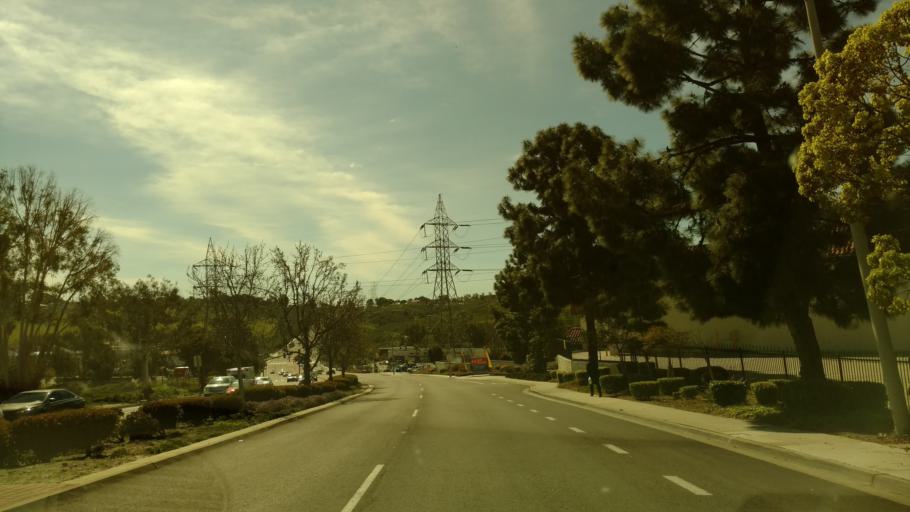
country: US
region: California
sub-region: San Diego County
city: Oceanside
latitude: 33.2035
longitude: -117.3334
